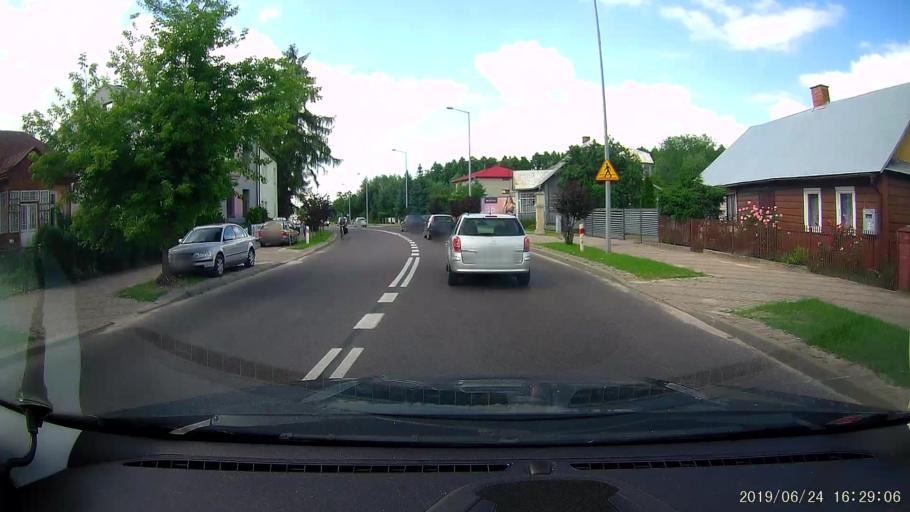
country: PL
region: Lublin Voivodeship
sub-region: Powiat tomaszowski
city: Tomaszow Lubelski
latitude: 50.4573
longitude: 23.4213
